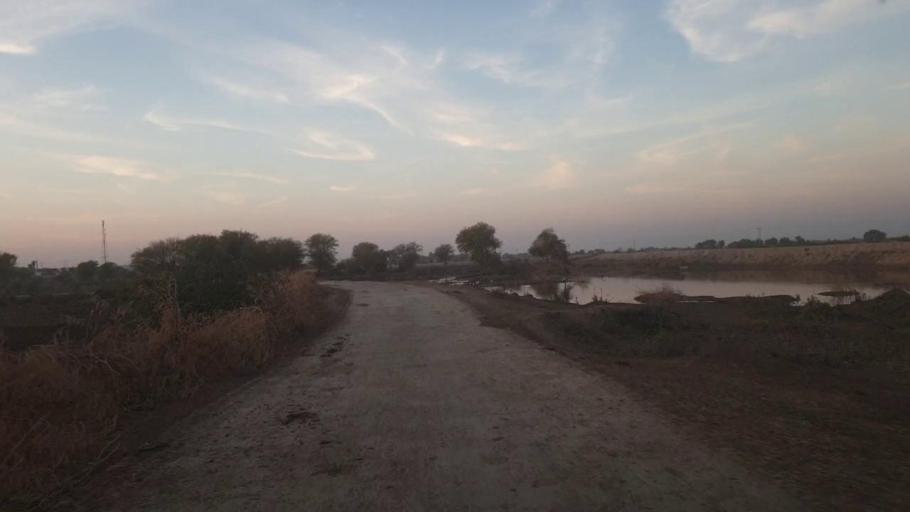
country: PK
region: Sindh
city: Hala
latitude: 25.7002
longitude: 68.3022
